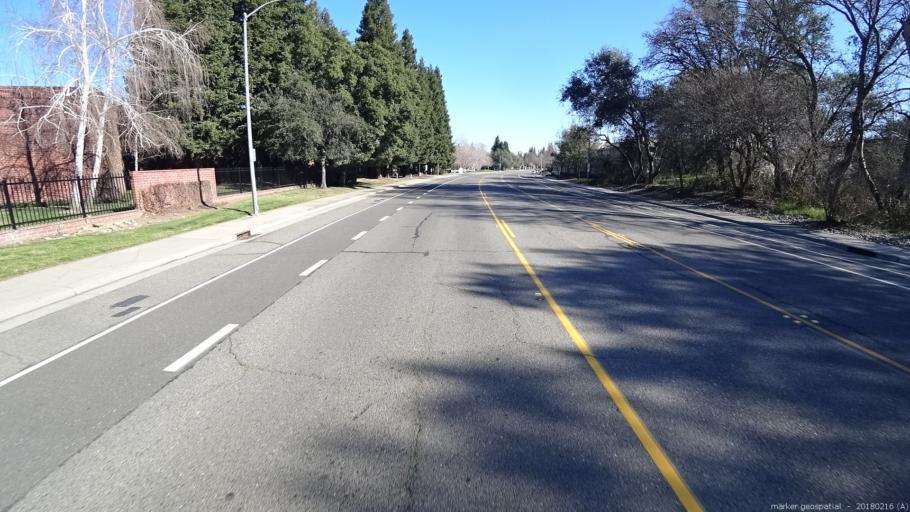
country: US
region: California
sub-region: Sacramento County
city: Gold River
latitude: 38.6245
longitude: -121.2632
